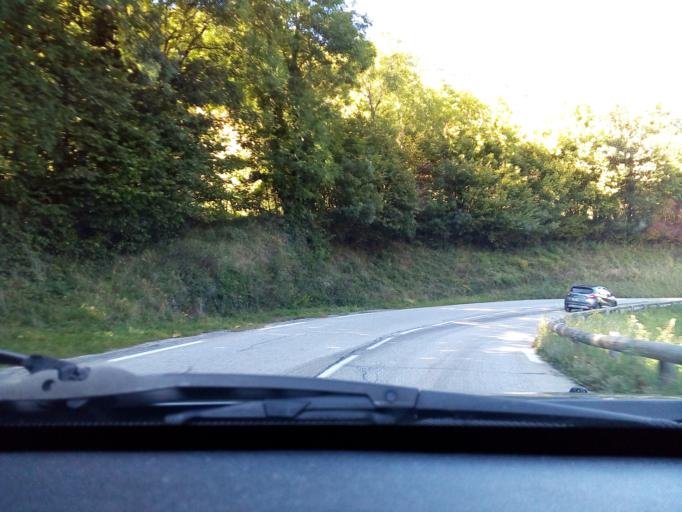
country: FR
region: Rhone-Alpes
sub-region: Departement de l'Isere
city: Sassenage
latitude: 45.1927
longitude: 5.6256
